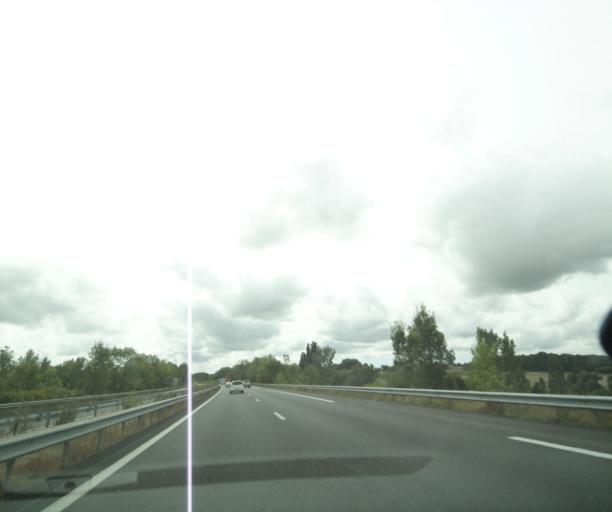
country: FR
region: Poitou-Charentes
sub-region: Departement de la Charente-Maritime
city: Mirambeau
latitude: 45.3834
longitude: -0.6026
